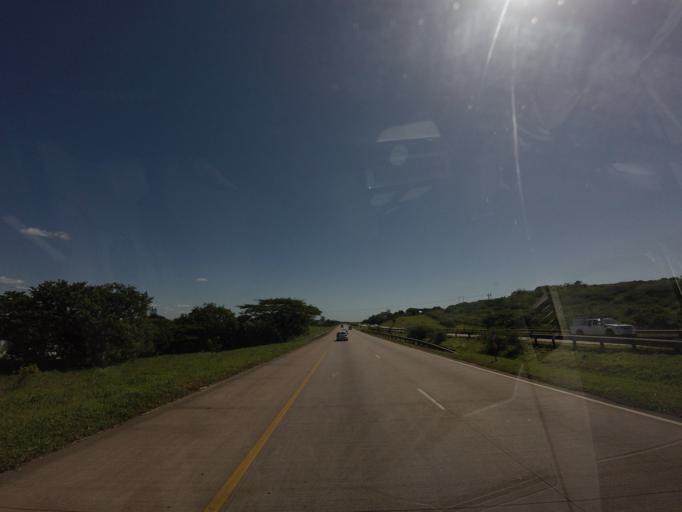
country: ZA
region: KwaZulu-Natal
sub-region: iLembe District Municipality
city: Ballitoville
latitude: -29.4893
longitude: 31.2194
